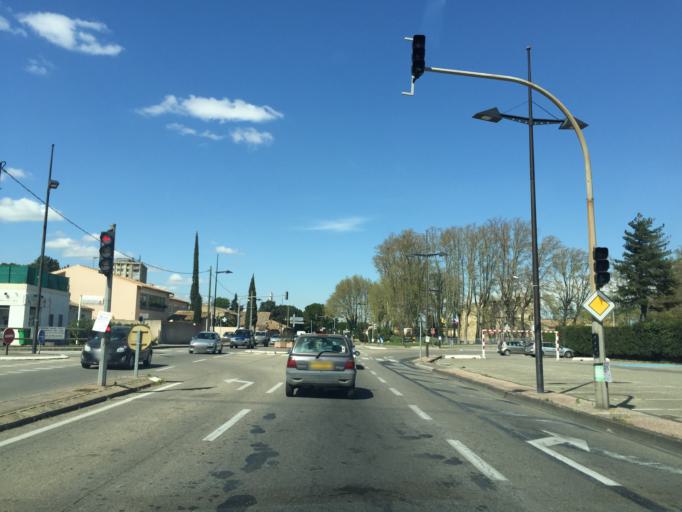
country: FR
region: Provence-Alpes-Cote d'Azur
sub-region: Departement du Vaucluse
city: Le Pontet
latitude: 43.9554
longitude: 4.8585
